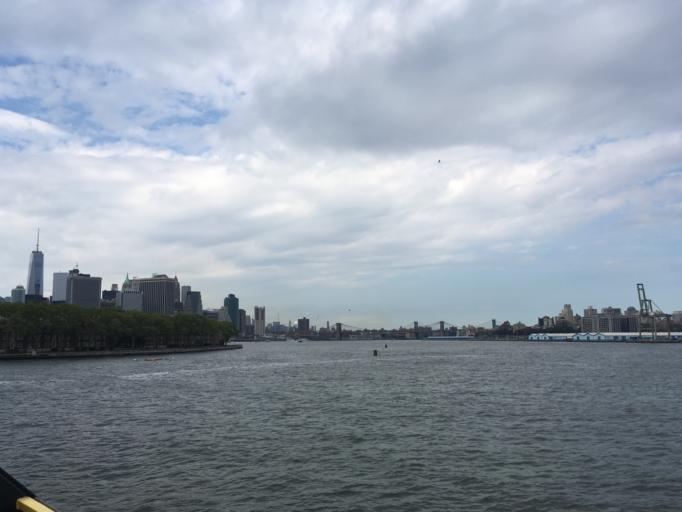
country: US
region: New York
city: New York City
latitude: 40.6855
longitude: -74.0141
